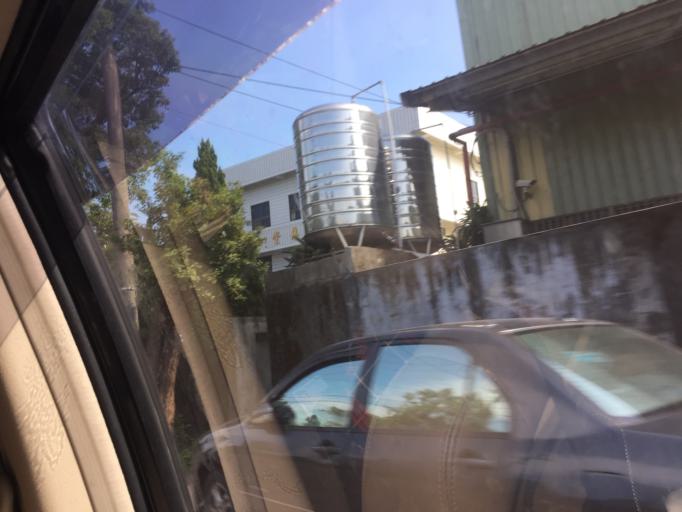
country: TW
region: Taiwan
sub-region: Taoyuan
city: Taoyuan
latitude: 24.9416
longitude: 121.3056
